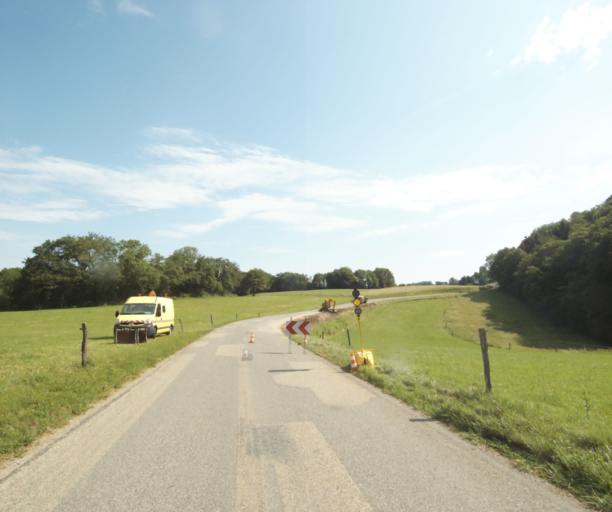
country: FR
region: Rhone-Alpes
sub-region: Departement de la Haute-Savoie
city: Lyaud
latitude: 46.3325
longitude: 6.5108
